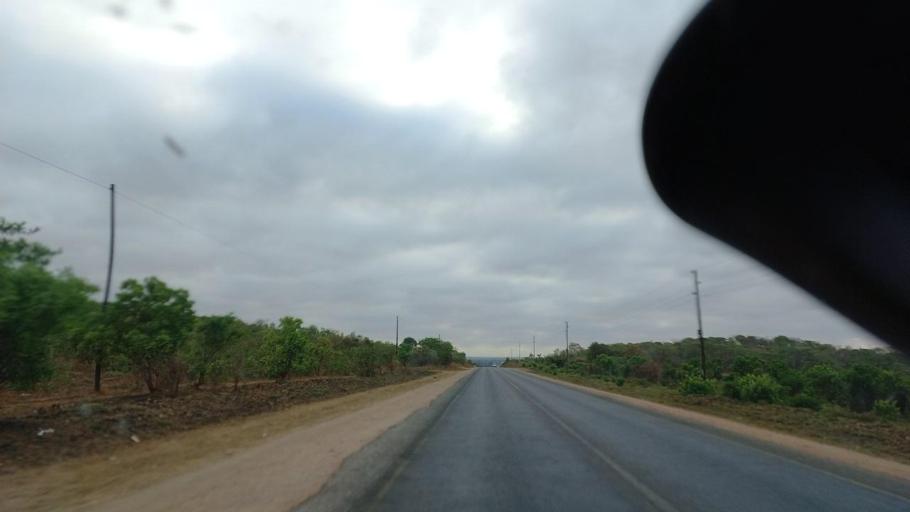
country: ZM
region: Lusaka
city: Chongwe
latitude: -15.3417
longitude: 28.6011
